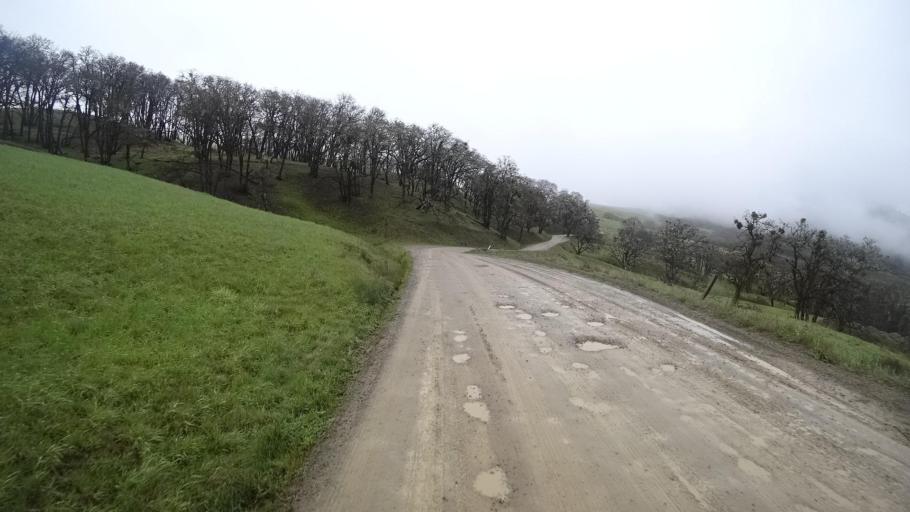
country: US
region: California
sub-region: Humboldt County
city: Westhaven-Moonstone
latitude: 41.1469
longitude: -123.8851
